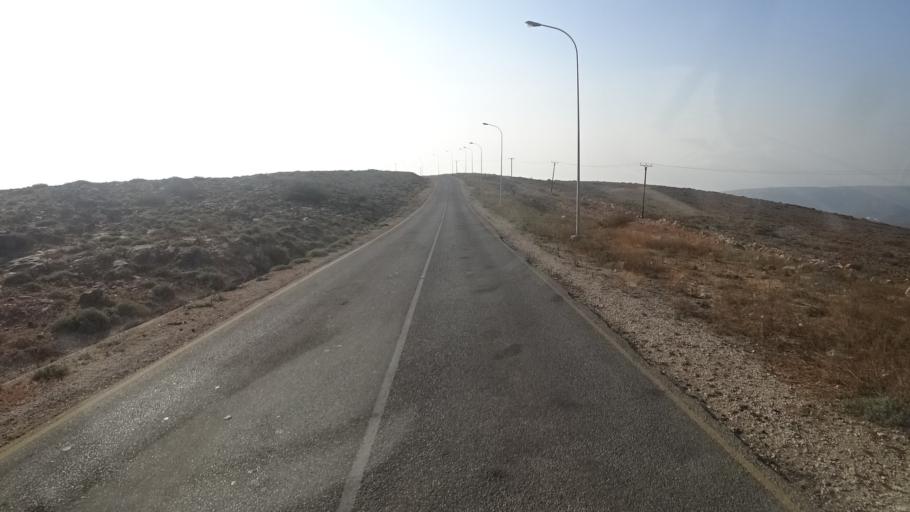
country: YE
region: Al Mahrah
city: Hawf
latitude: 16.7653
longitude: 53.2321
